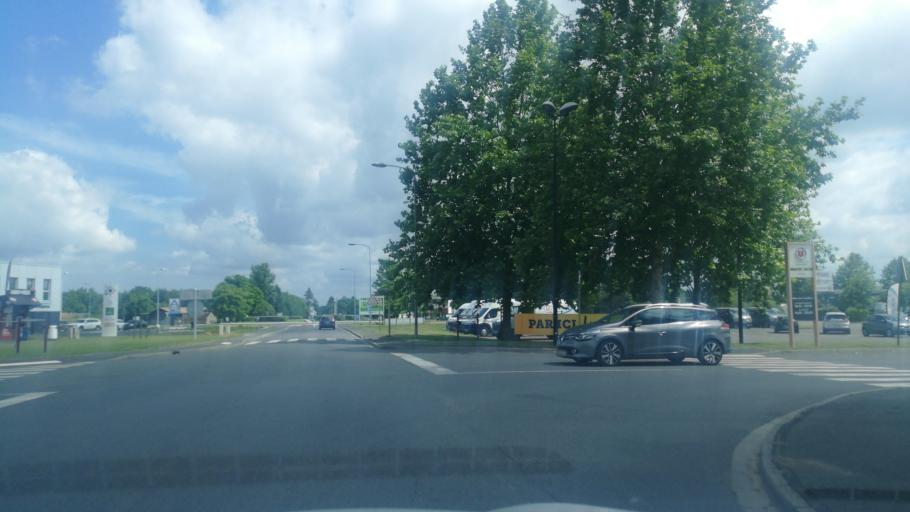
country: FR
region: Centre
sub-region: Departement du Loir-et-Cher
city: Contres
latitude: 47.4299
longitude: 1.4341
